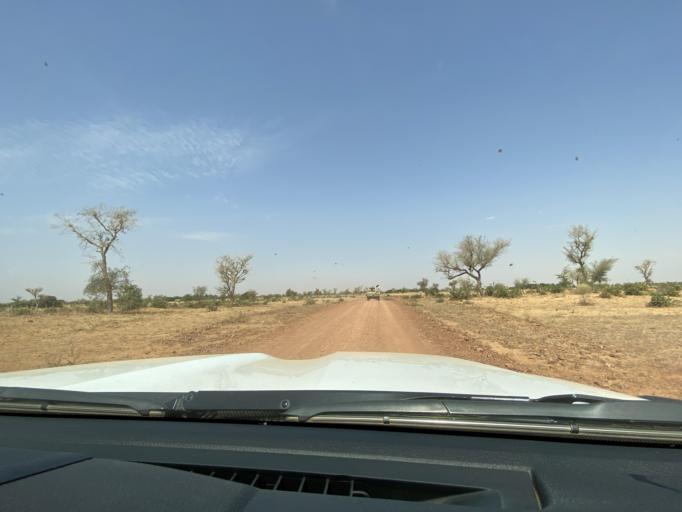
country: NE
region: Dosso
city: Birnin Gaoure
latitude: 13.2340
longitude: 2.8684
